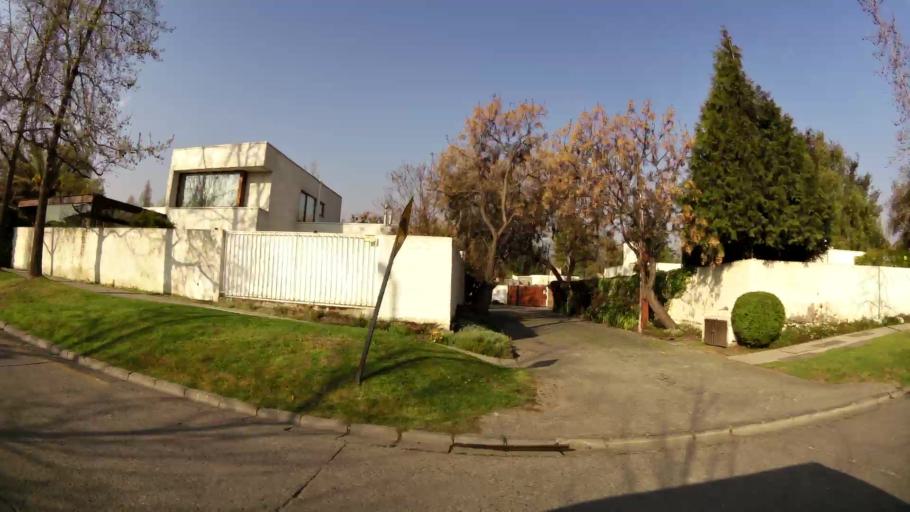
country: CL
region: Santiago Metropolitan
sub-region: Provincia de Santiago
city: Villa Presidente Frei, Nunoa, Santiago, Chile
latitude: -33.3586
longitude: -70.5339
